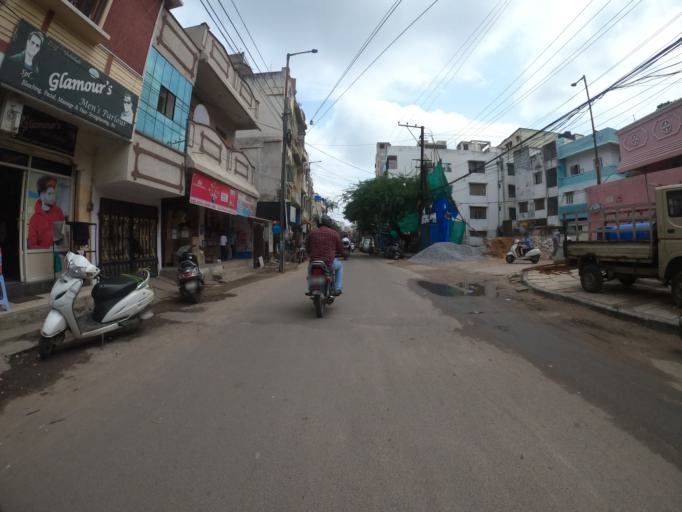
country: IN
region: Telangana
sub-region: Hyderabad
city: Hyderabad
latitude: 17.3952
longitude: 78.4174
